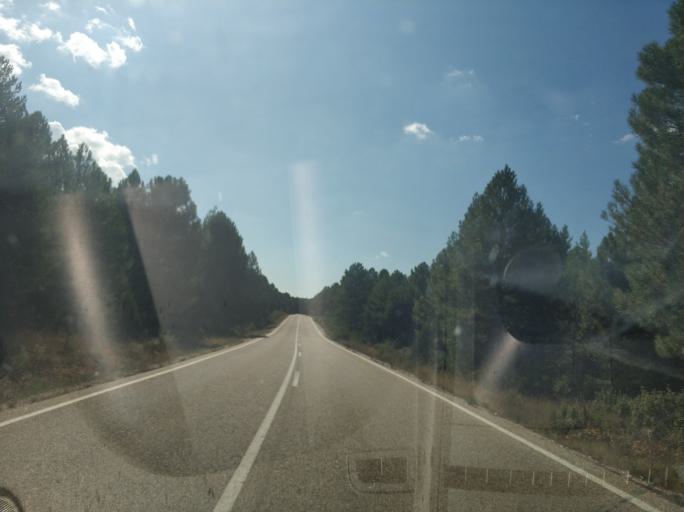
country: ES
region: Castille and Leon
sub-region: Provincia de Soria
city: Herrera de Soria
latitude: 41.7645
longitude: -3.0329
